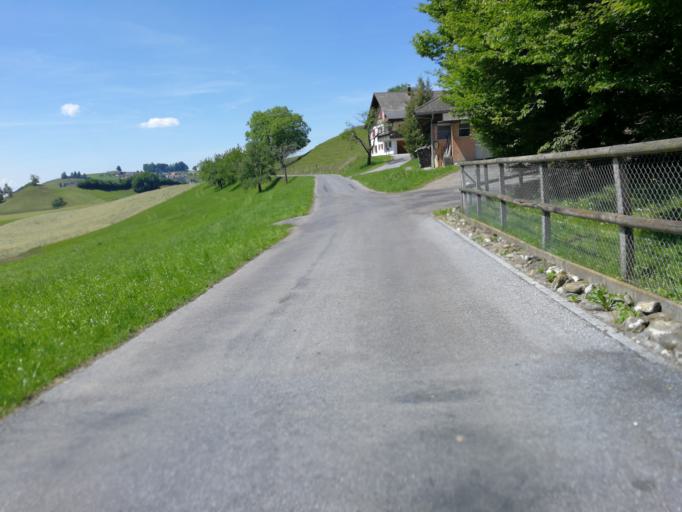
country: CH
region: Zurich
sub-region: Bezirk Horgen
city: Waedenswil / Hangenmoos
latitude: 47.2103
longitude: 8.6320
